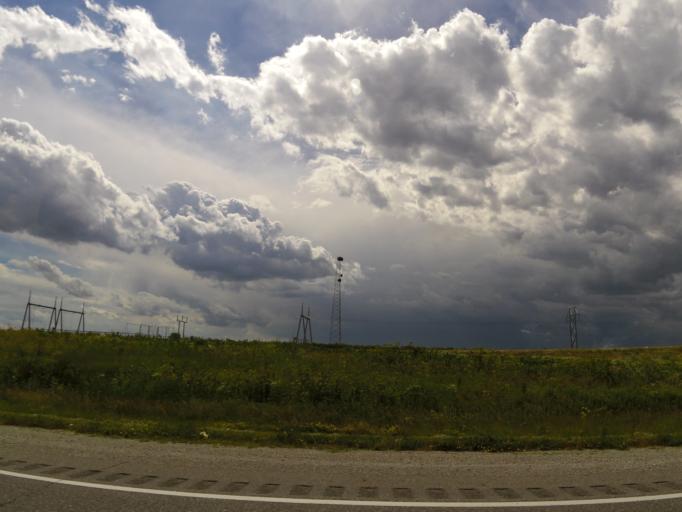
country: US
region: Iowa
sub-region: Washington County
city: Washington
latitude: 41.3358
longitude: -91.5527
